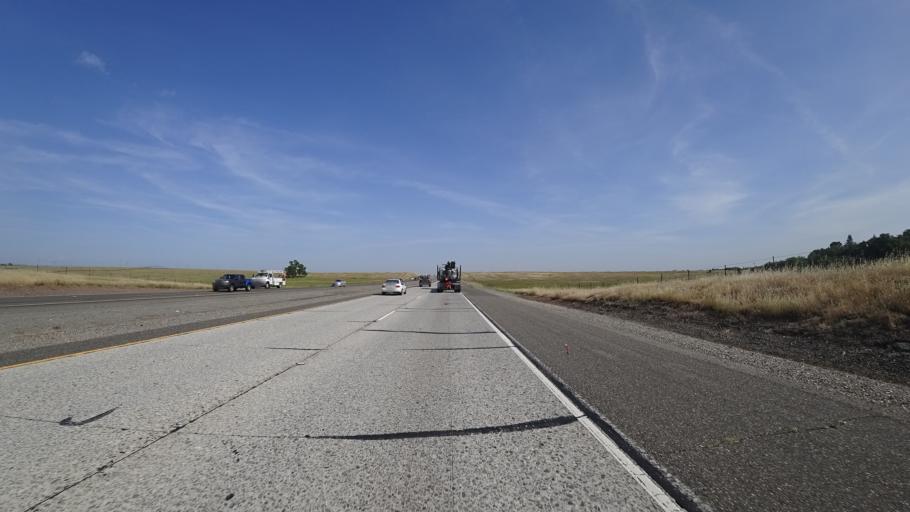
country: US
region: California
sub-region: Butte County
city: Durham
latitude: 39.6805
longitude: -121.7629
